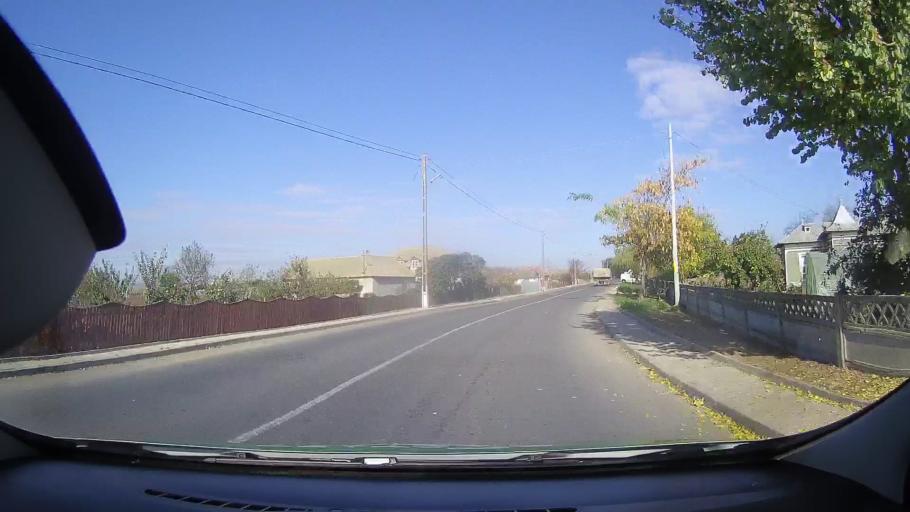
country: RO
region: Tulcea
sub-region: Comuna Mahmudia
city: Mahmudia
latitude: 45.0090
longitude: 29.0553
